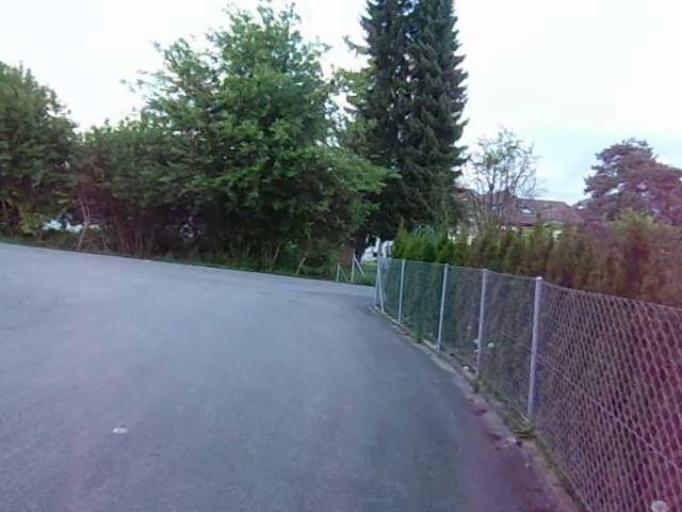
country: CH
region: Zurich
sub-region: Bezirk Hinwil
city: Rueti / Dorfzentrum, Suedl. Teil
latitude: 47.2503
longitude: 8.8614
